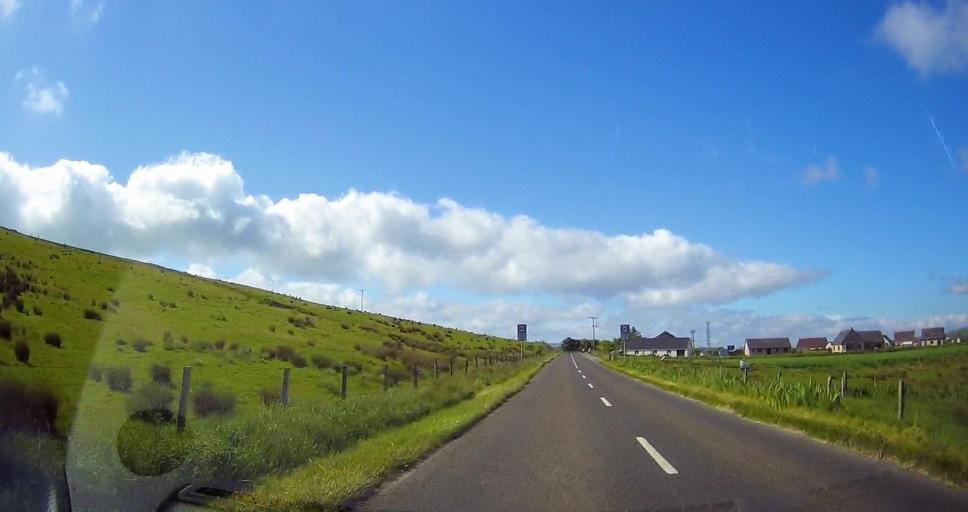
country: GB
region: Scotland
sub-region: Orkney Islands
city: Orkney
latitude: 58.9639
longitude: -2.9669
